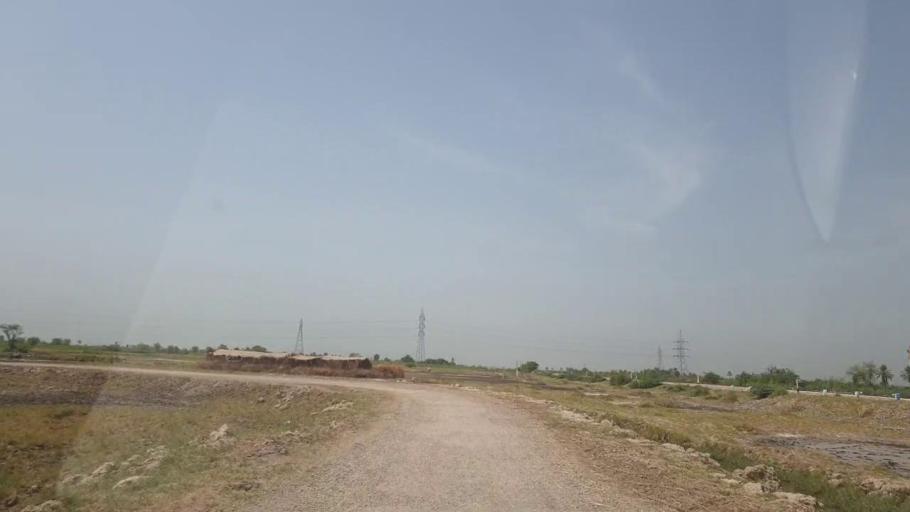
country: PK
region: Sindh
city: Gambat
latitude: 27.3168
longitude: 68.5348
